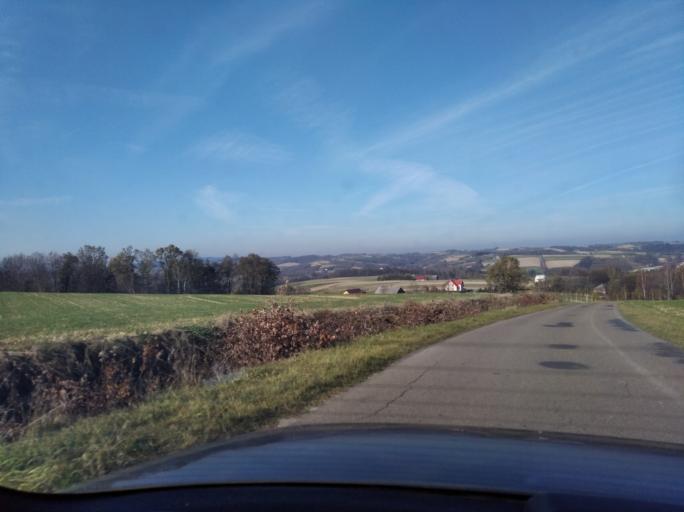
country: PL
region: Subcarpathian Voivodeship
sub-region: Powiat ropczycko-sedziszowski
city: Wielopole Skrzynskie
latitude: 49.9174
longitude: 21.5651
